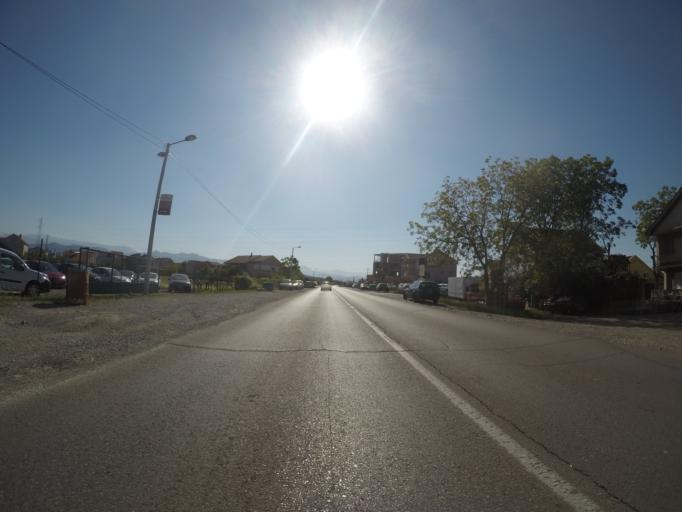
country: ME
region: Podgorica
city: Podgorica
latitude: 42.4386
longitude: 19.2234
